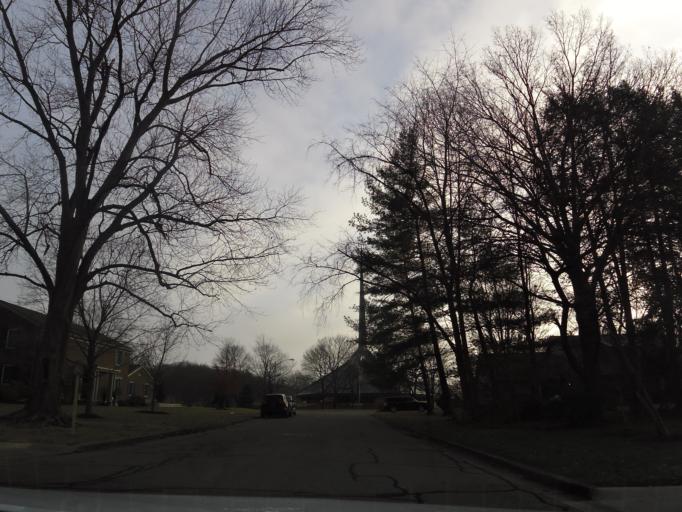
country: US
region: Indiana
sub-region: Bartholomew County
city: Columbus
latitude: 39.2298
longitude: -85.9181
